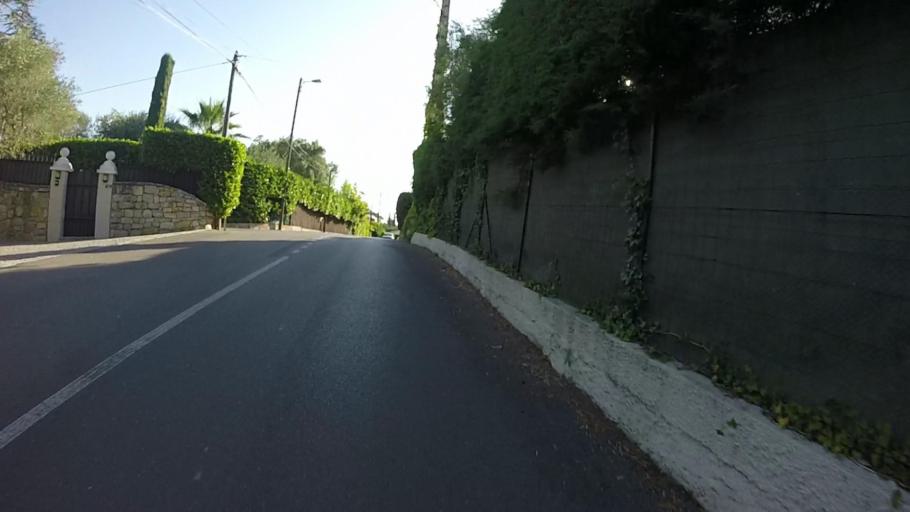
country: FR
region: Provence-Alpes-Cote d'Azur
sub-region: Departement des Alpes-Maritimes
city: Mougins
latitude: 43.6097
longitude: 7.0061
